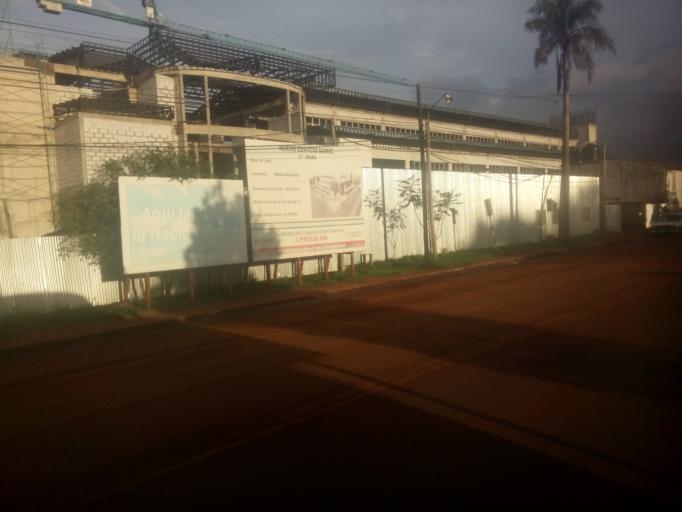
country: AR
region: Misiones
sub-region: Departamento de Obera
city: Obera
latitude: -27.4921
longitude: -55.1452
